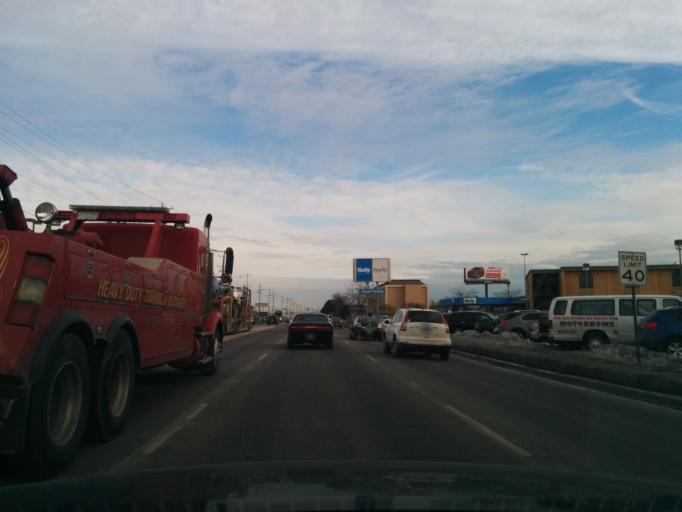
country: US
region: Illinois
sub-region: Cook County
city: Schiller Park
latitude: 41.9471
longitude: -87.8855
